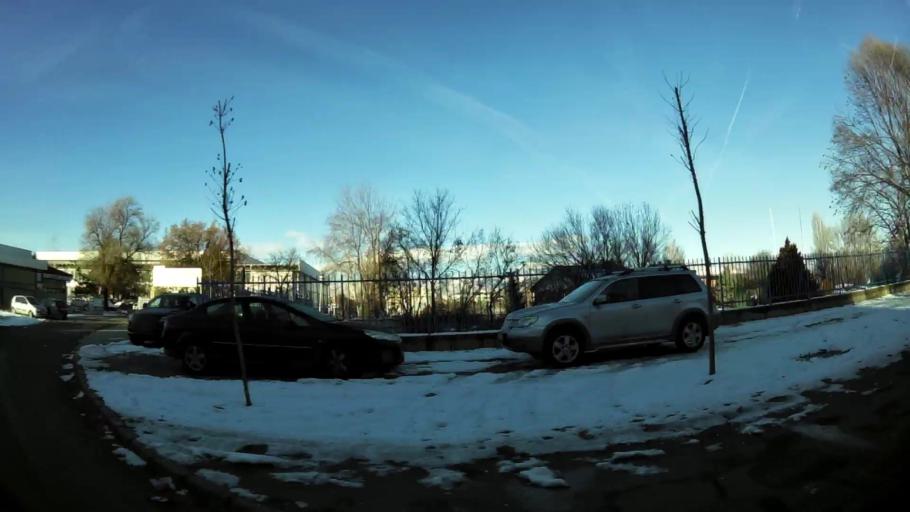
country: MK
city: Krushopek
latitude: 42.0089
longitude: 21.3844
